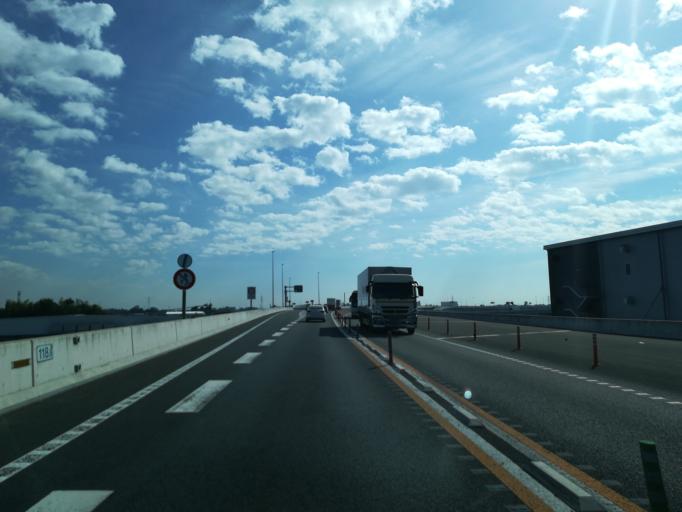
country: JP
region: Ibaraki
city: Sakai
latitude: 36.0990
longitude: 139.7595
